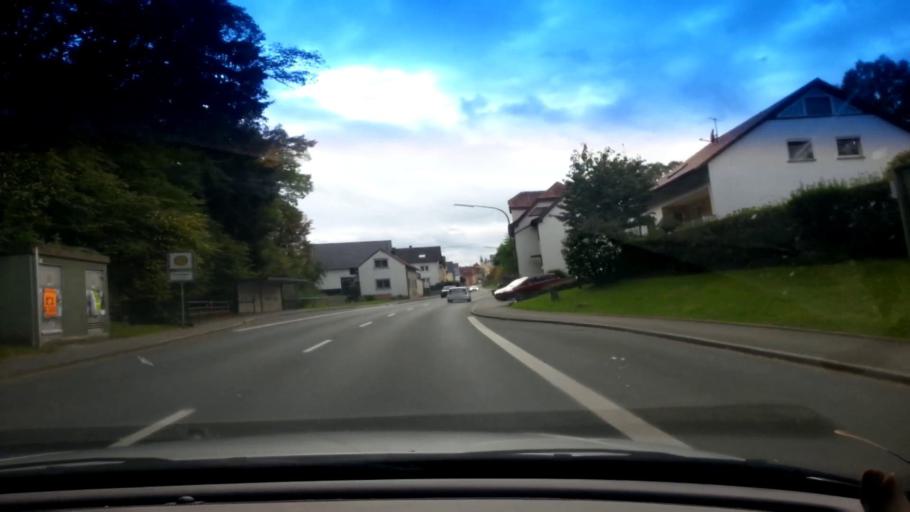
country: DE
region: Bavaria
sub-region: Upper Franconia
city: Oberhaid
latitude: 49.9143
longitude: 10.8119
